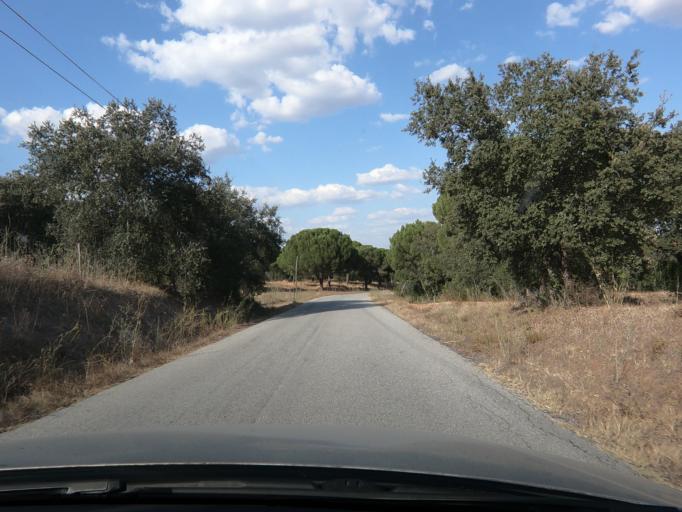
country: PT
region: Setubal
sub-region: Alcacer do Sal
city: Alcacer do Sal
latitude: 38.2440
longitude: -8.3636
